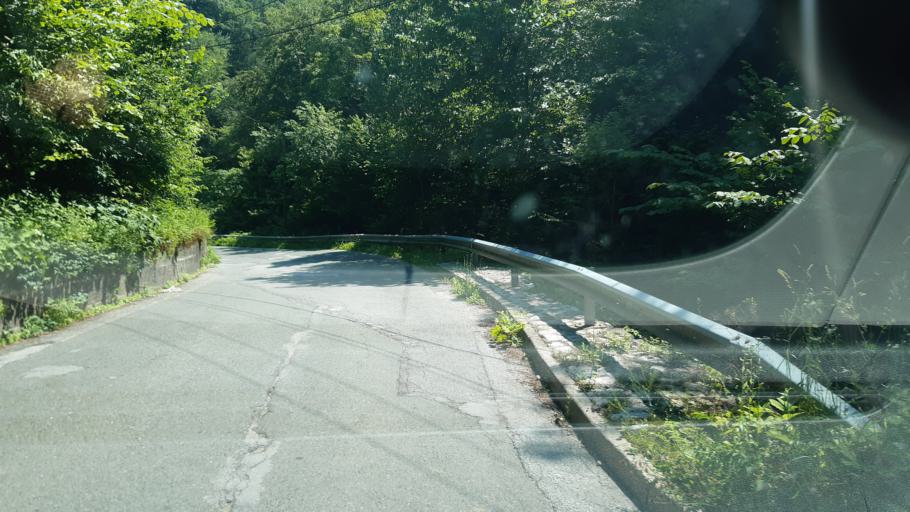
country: SI
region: Cerklje na Gorenjskem
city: Cerklje na Gorenjskem
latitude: 46.2793
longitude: 14.4970
